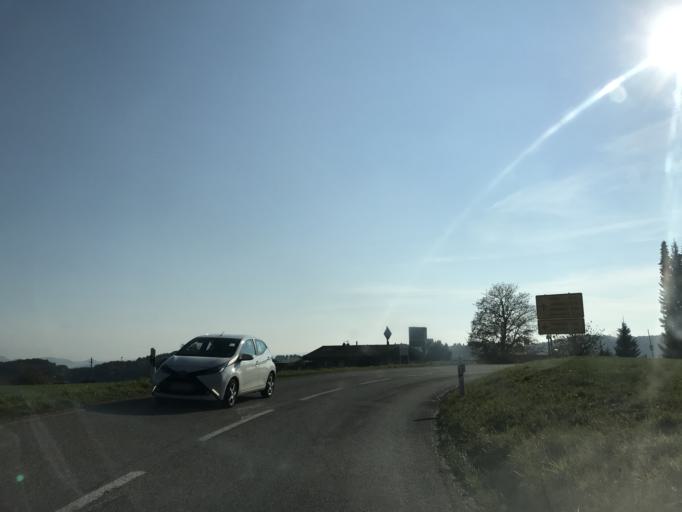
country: DE
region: Baden-Wuerttemberg
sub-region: Freiburg Region
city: Gorwihl
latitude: 47.6339
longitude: 8.0710
